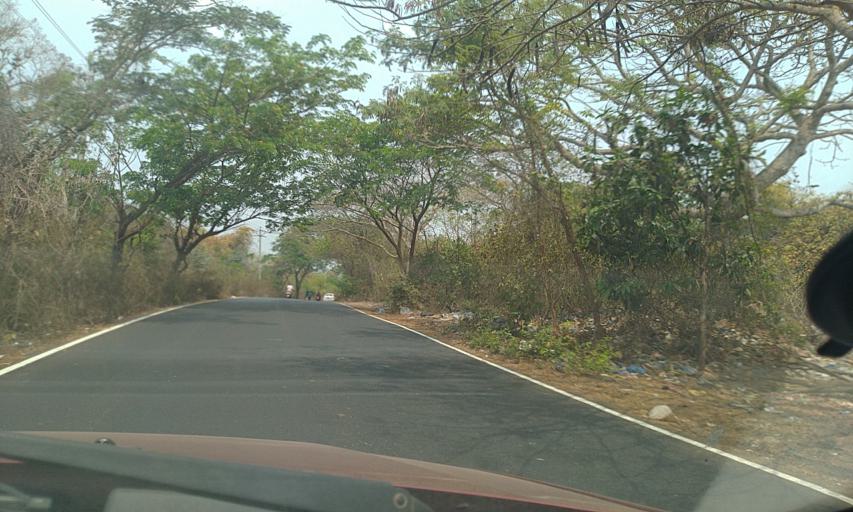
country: IN
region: Goa
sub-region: North Goa
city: Mapuca
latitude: 15.6096
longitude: 73.7970
